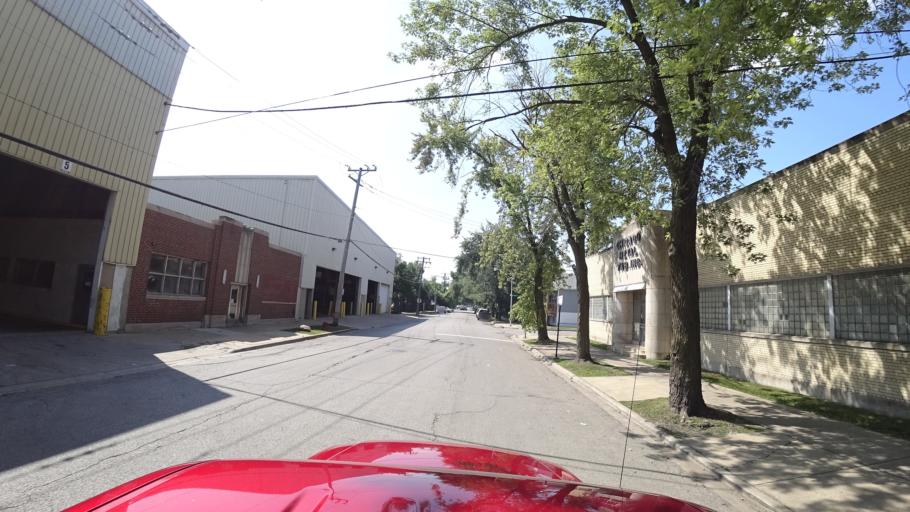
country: US
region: Illinois
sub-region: Cook County
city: Chicago
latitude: 41.8260
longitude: -87.6899
